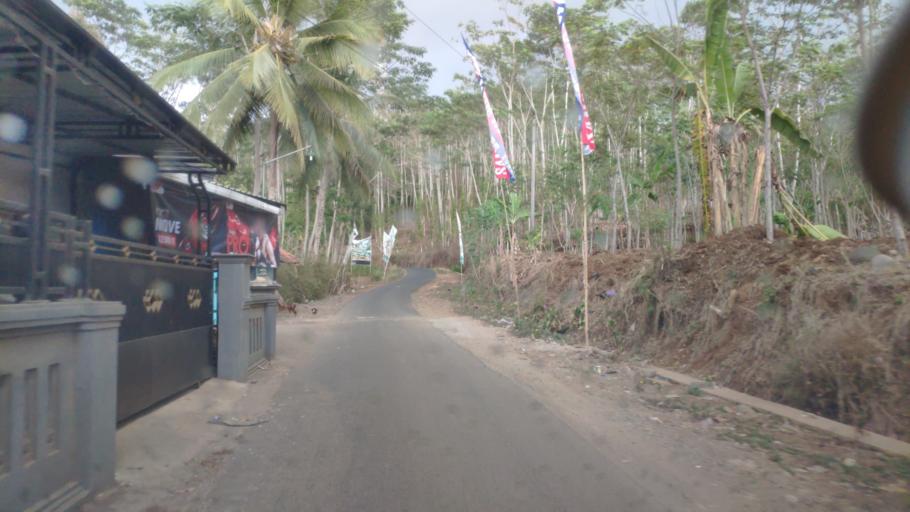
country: ID
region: Central Java
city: Purbalingga
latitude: -7.3499
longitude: 109.5451
